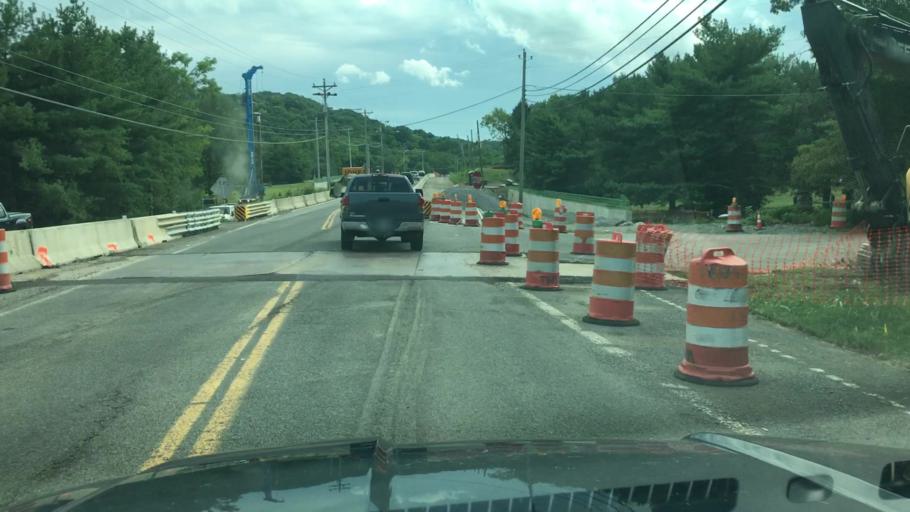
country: US
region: Tennessee
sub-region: Williamson County
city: Brentwood Estates
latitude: 35.9873
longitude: -86.8163
